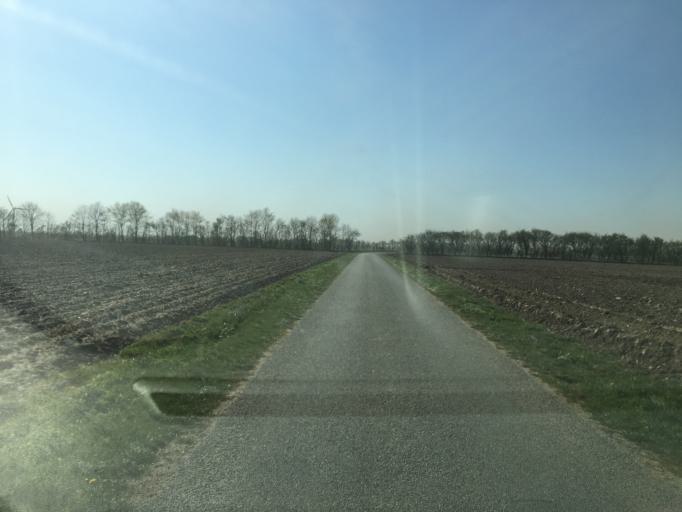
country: DK
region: South Denmark
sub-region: Aabenraa Kommune
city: Rodekro
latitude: 55.1129
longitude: 9.1898
